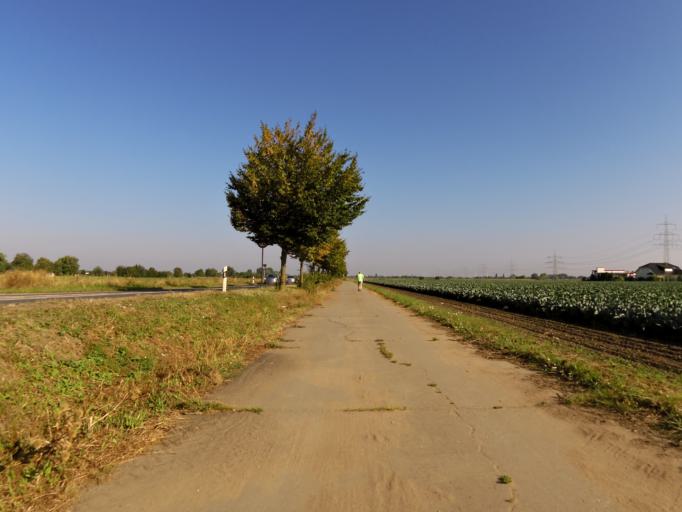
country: DE
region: Rheinland-Pfalz
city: Maxdorf
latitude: 49.4840
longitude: 8.3046
